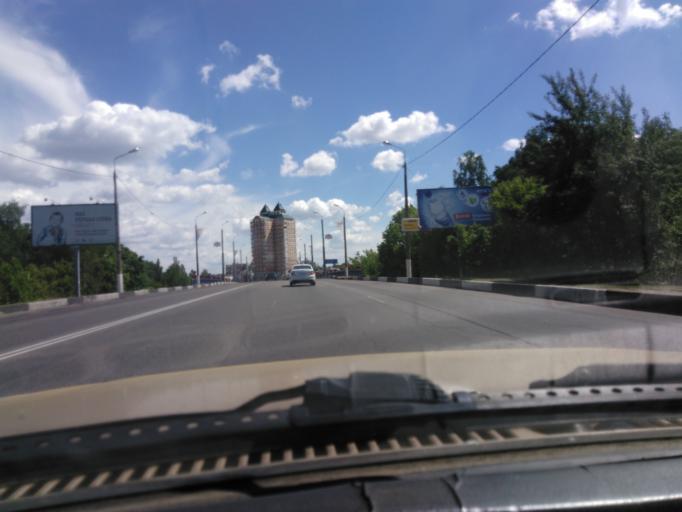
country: BY
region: Mogilev
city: Mahilyow
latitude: 53.9150
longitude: 30.3157
